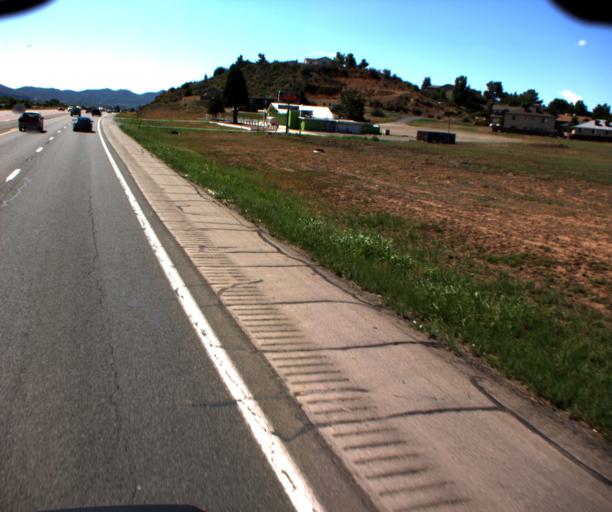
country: US
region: Arizona
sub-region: Yavapai County
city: Dewey-Humboldt
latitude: 34.5599
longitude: -112.2576
